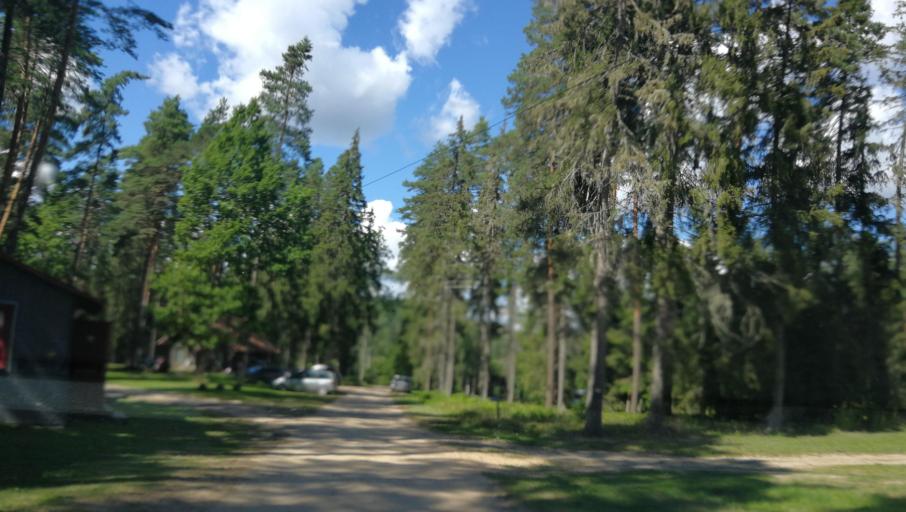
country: LV
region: Cesu Rajons
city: Cesis
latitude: 57.2934
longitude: 25.2148
